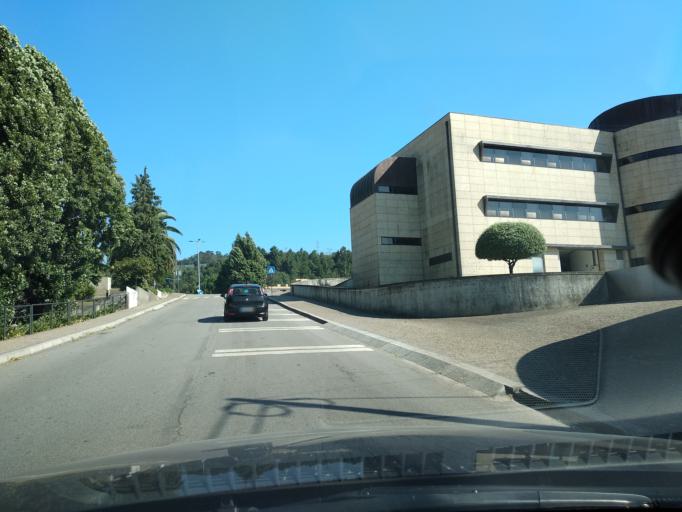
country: PT
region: Porto
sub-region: Paredes
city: Rebordosa
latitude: 41.2206
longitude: -8.4127
